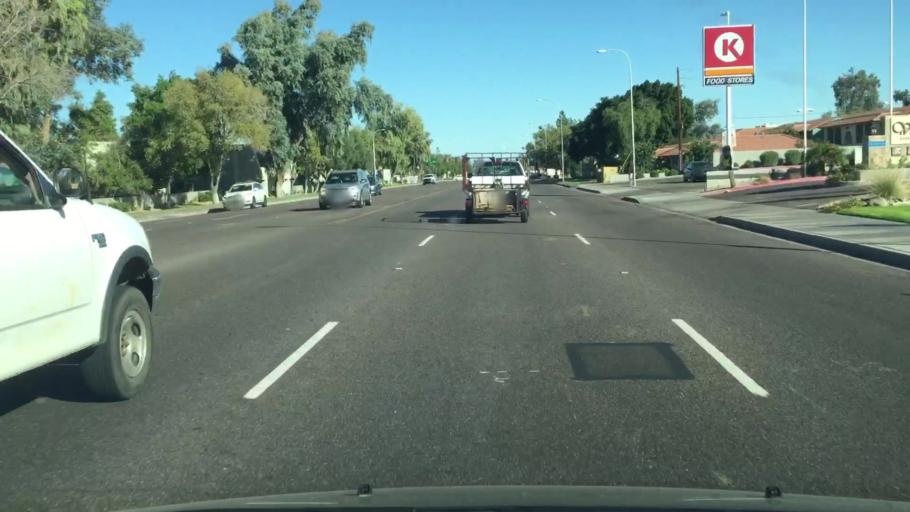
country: US
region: Arizona
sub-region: Maricopa County
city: Guadalupe
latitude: 33.3782
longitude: -111.9555
